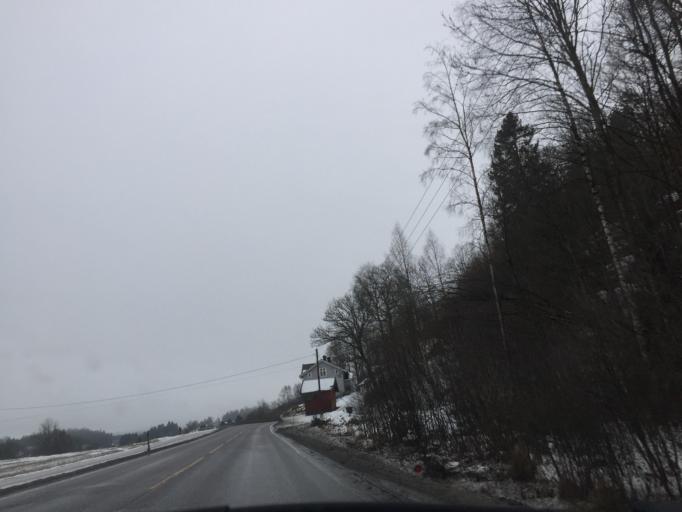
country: NO
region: Akershus
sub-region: Frogn
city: Drobak
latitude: 59.6817
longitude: 10.6659
